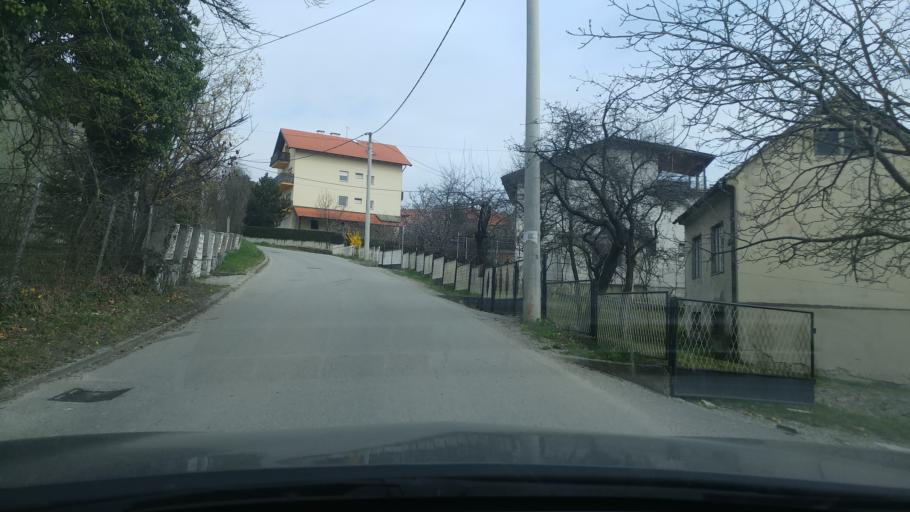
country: HR
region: Grad Zagreb
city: Stenjevec
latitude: 45.8383
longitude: 15.9226
